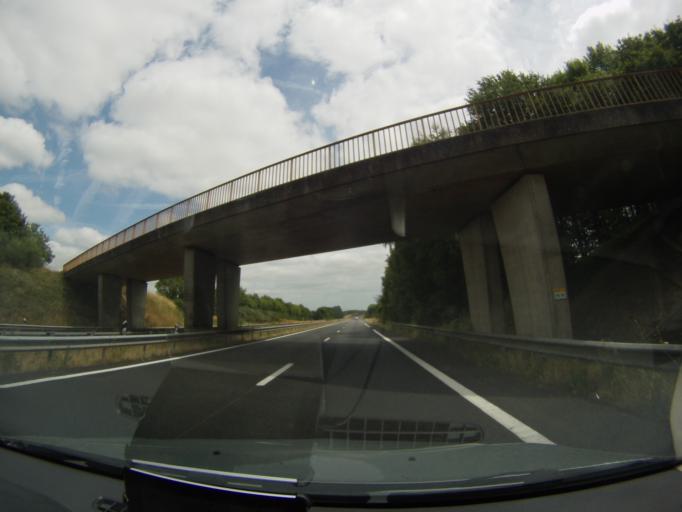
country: FR
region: Pays de la Loire
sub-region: Departement de Maine-et-Loire
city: Villedieu-la-Blouere
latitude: 47.1194
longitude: -1.0825
